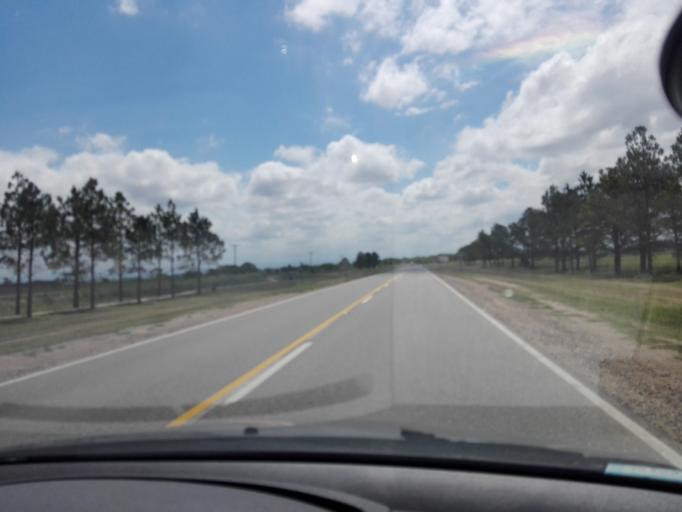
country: AR
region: Cordoba
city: Toledo
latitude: -31.6495
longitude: -64.0957
